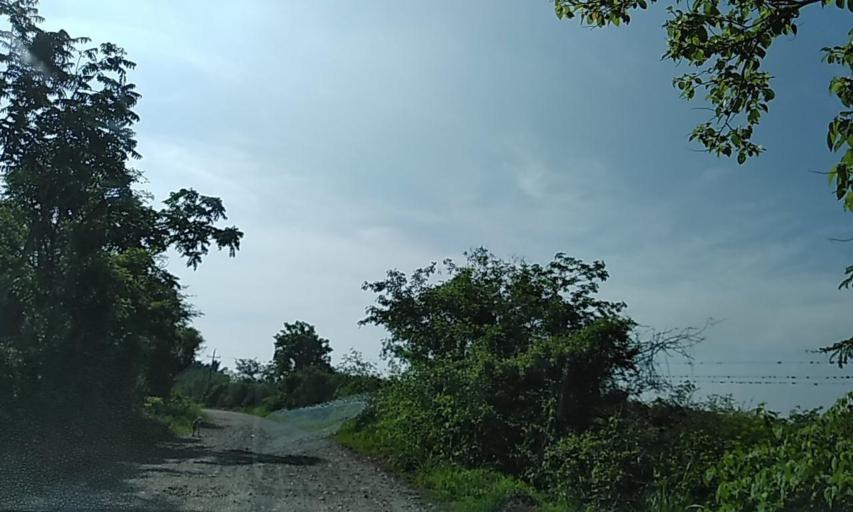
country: MX
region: Veracruz
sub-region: Emiliano Zapata
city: Plan del Rio
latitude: 19.4518
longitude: -96.6814
